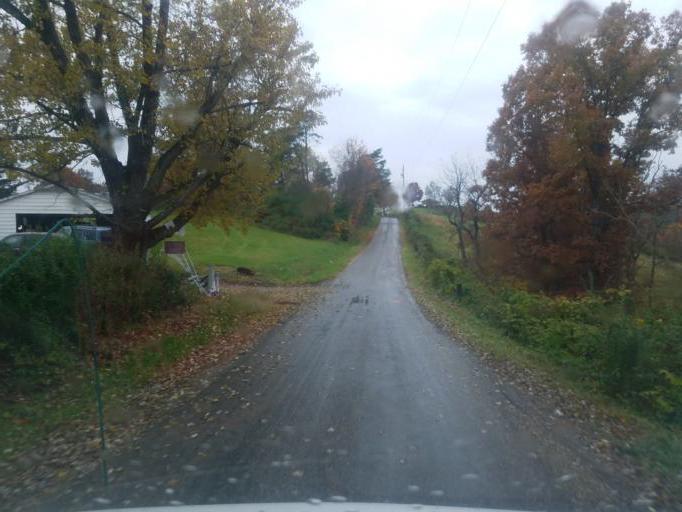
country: US
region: Ohio
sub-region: Washington County
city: Belpre
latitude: 39.3208
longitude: -81.6066
